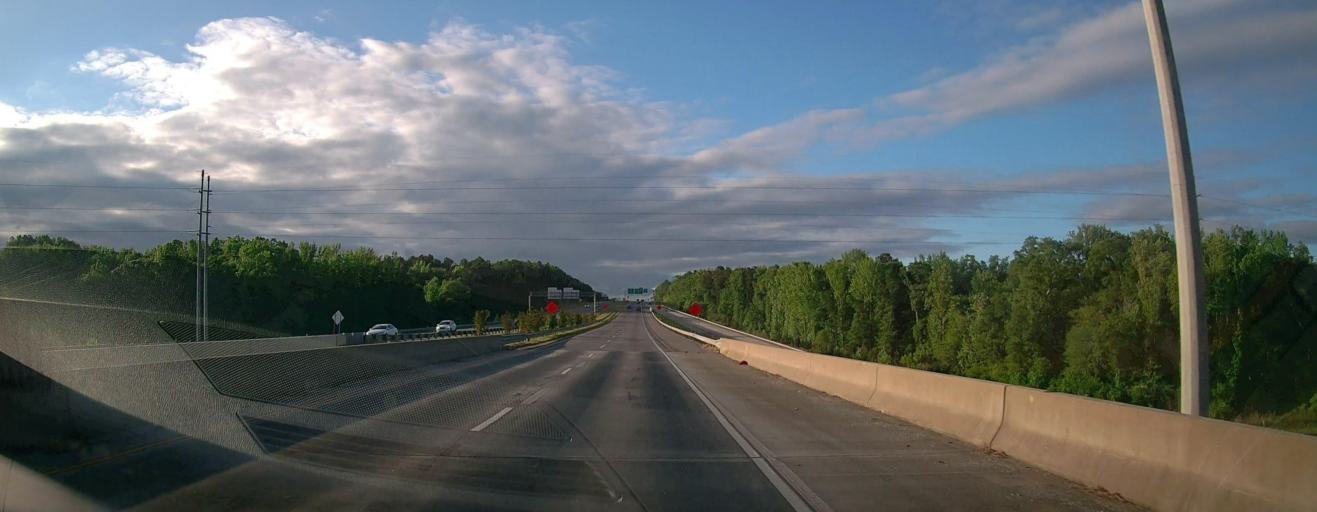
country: US
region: Georgia
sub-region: Clarke County
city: Athens
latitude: 33.9636
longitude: -83.3527
